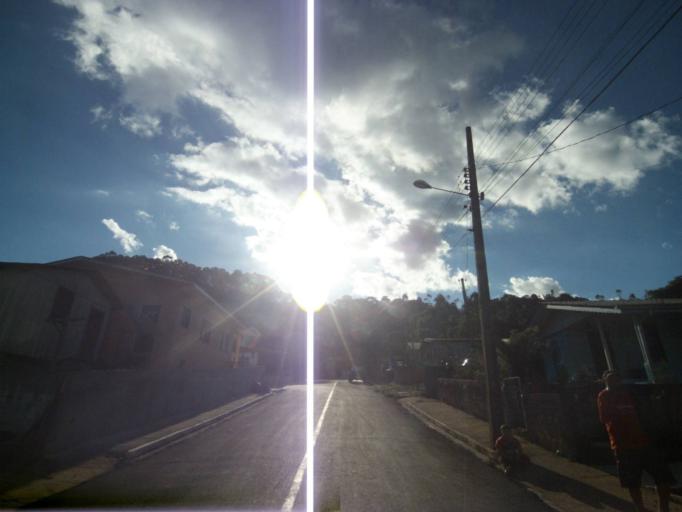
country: BR
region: Parana
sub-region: Uniao Da Vitoria
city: Uniao da Vitoria
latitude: -26.1664
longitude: -51.5385
